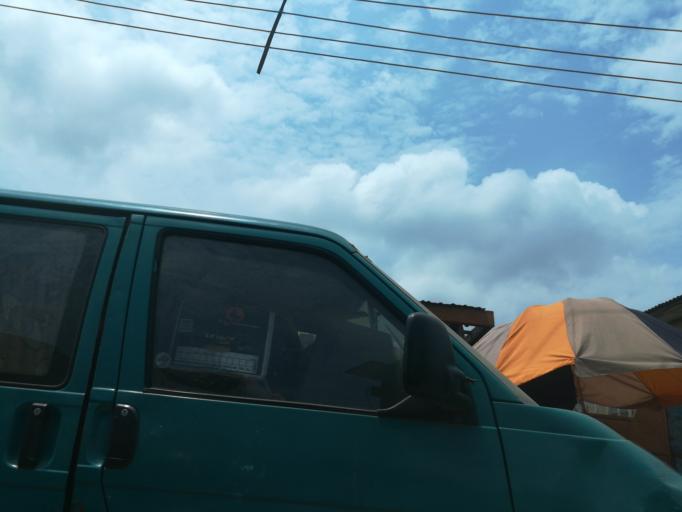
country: NG
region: Lagos
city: Oshodi
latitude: 6.5514
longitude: 3.3281
